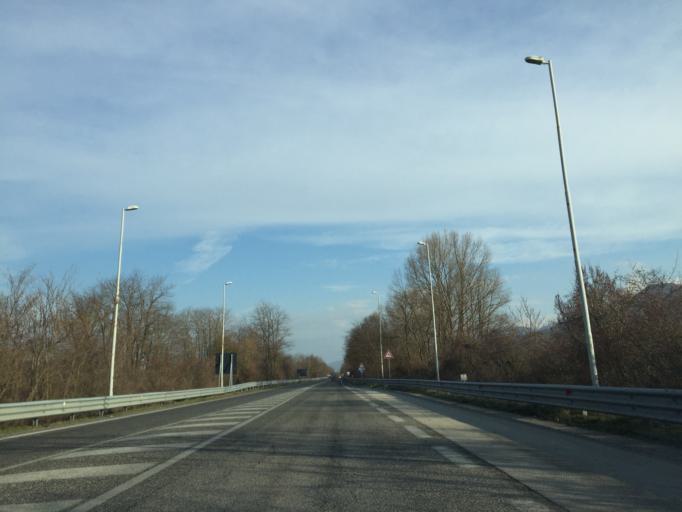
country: IT
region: Molise
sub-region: Provincia di Campobasso
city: San Massimo
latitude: 41.5101
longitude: 14.4370
